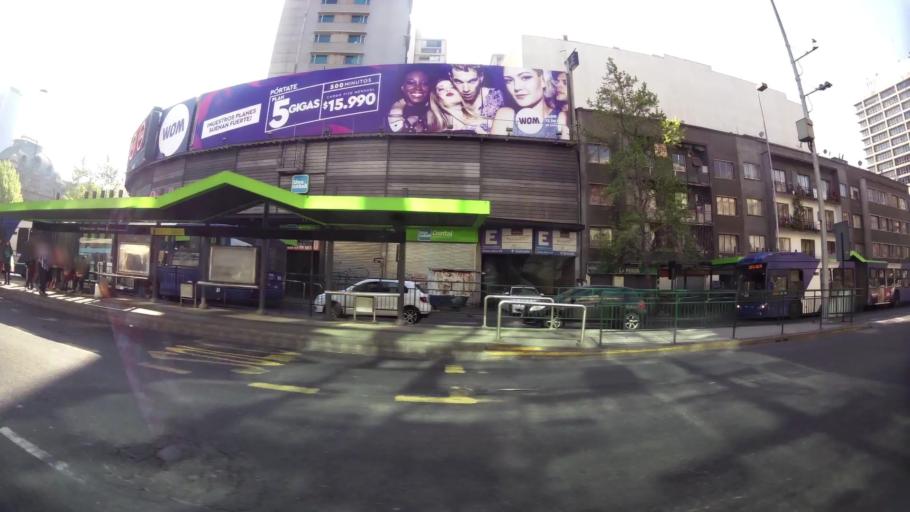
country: CL
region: Santiago Metropolitan
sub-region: Provincia de Santiago
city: Santiago
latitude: -33.4433
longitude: -70.6460
